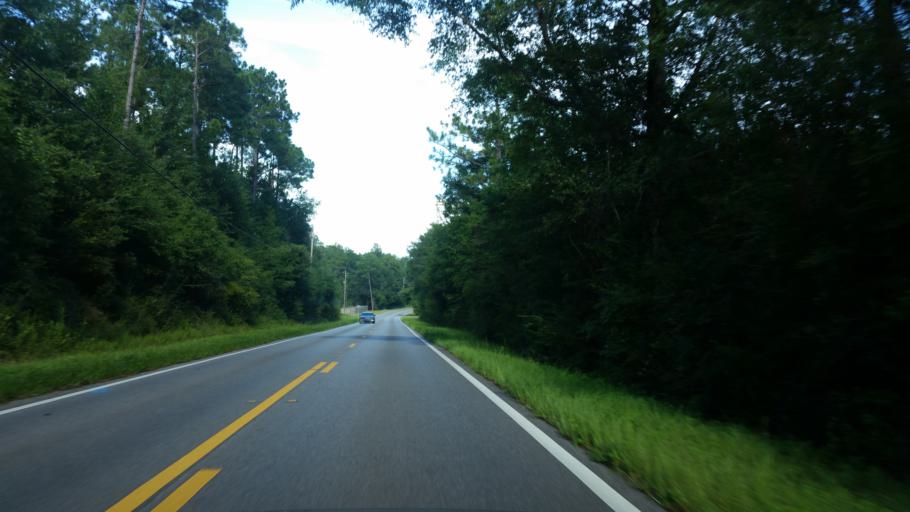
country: US
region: Florida
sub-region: Santa Rosa County
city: Pace
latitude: 30.6249
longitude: -87.1163
